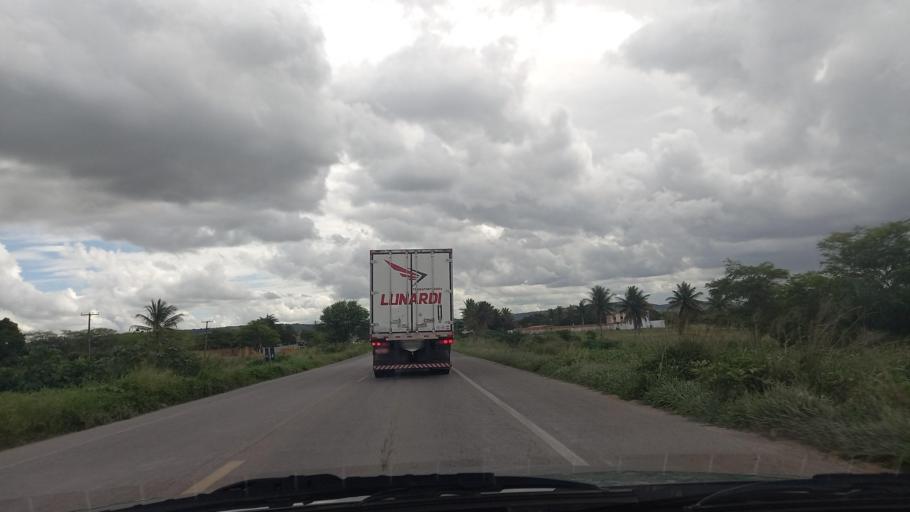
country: BR
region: Pernambuco
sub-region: Lajedo
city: Lajedo
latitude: -8.6617
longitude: -36.3450
